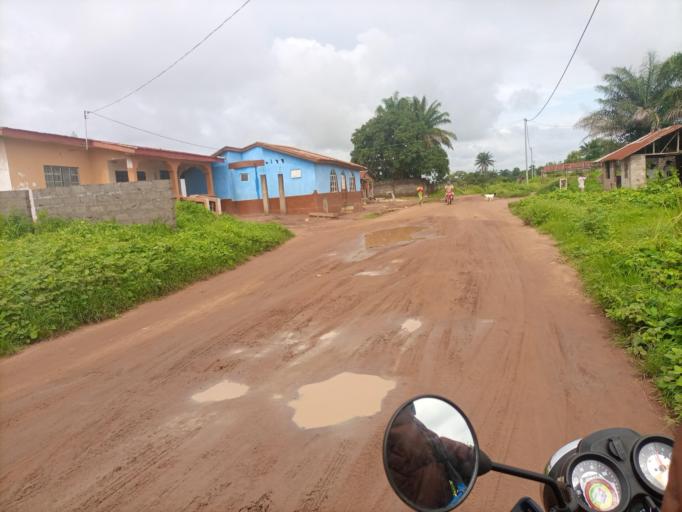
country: SL
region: Northern Province
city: Masoyila
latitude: 8.5961
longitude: -13.1658
